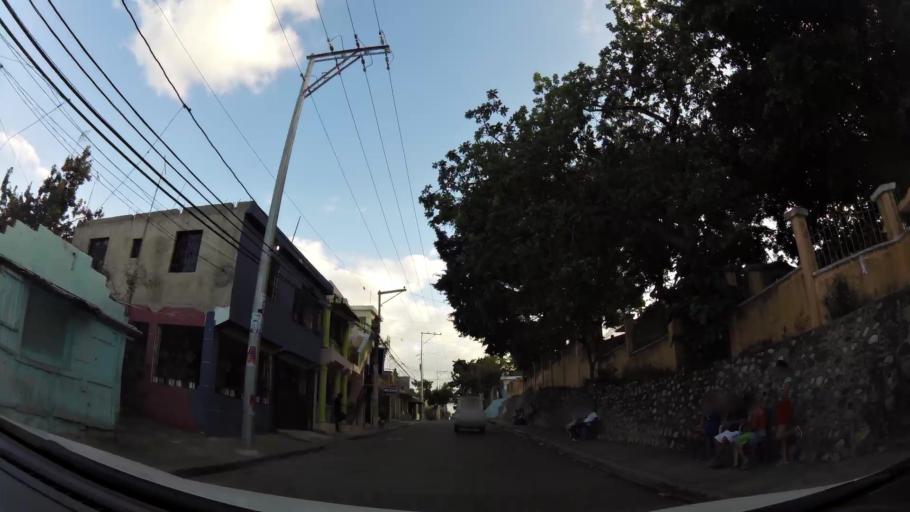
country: DO
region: Nacional
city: La Agustina
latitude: 18.5431
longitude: -69.9263
